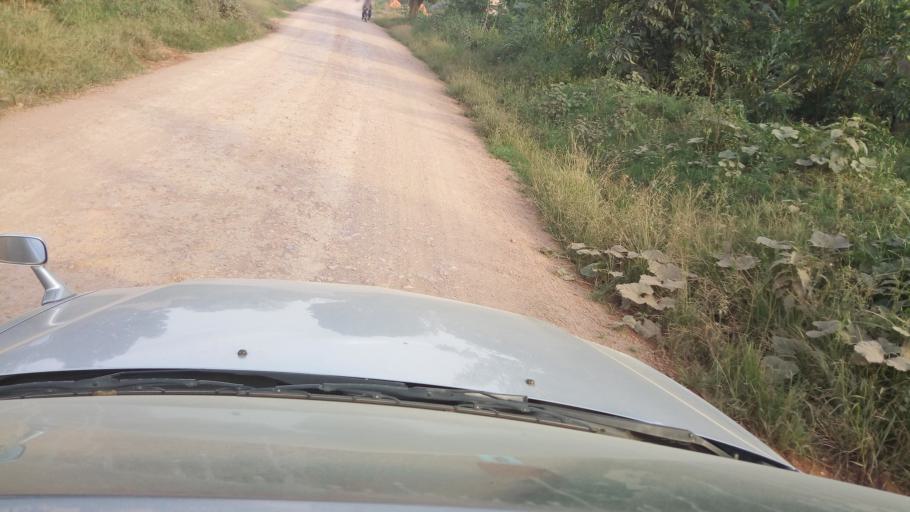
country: UG
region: Central Region
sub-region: Kiboga District
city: Kiboga
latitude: 0.7103
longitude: 31.7604
